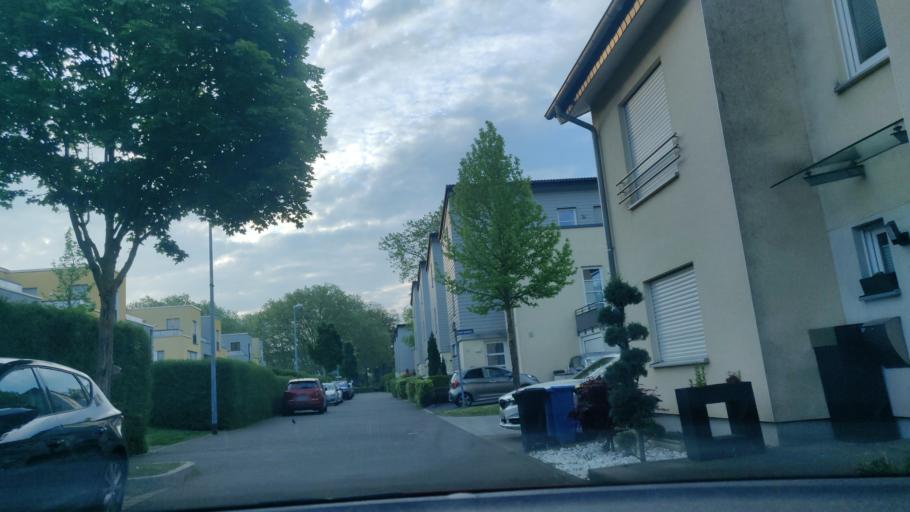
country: DE
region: North Rhine-Westphalia
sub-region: Regierungsbezirk Dusseldorf
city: Velbert
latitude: 51.3834
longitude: 7.0729
